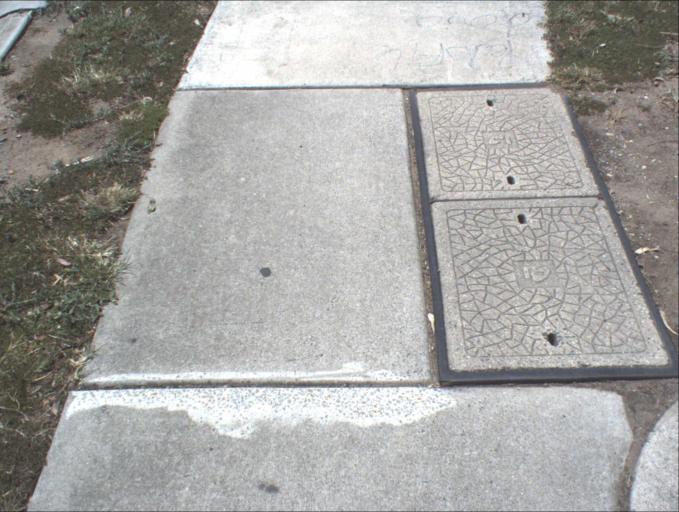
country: AU
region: Queensland
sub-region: Logan
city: Beenleigh
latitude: -27.7007
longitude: 153.2135
